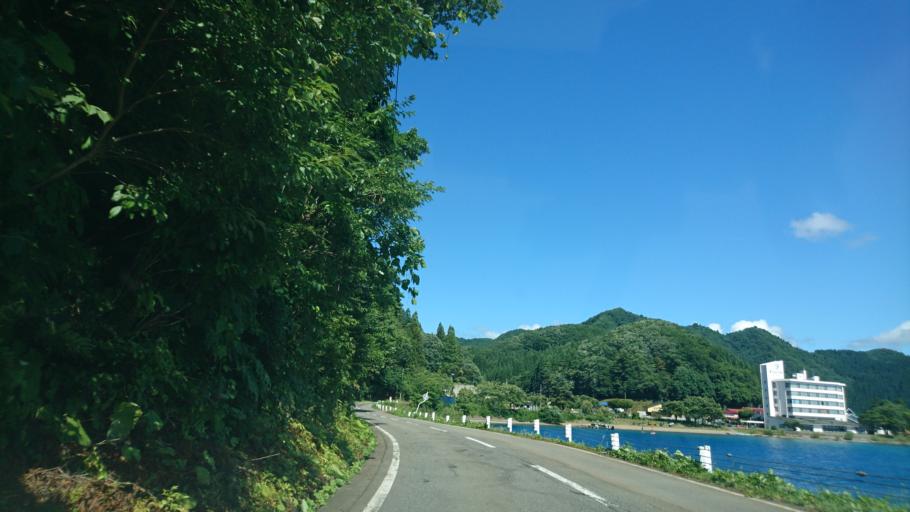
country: JP
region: Akita
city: Kakunodatemachi
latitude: 39.7105
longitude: 140.6362
